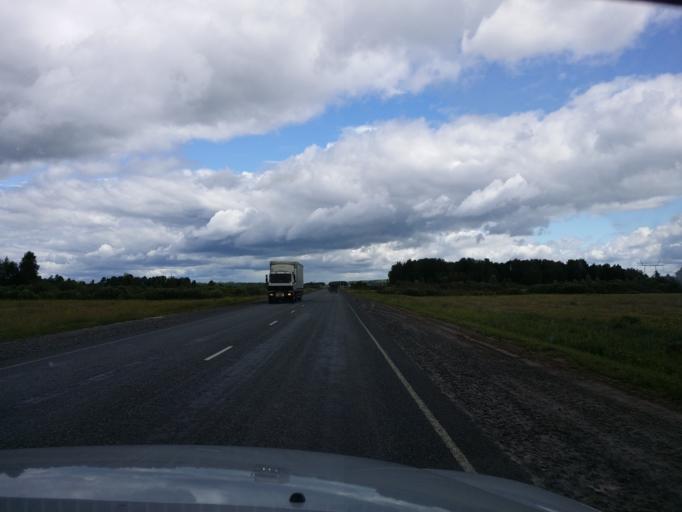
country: RU
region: Tjumen
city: Sumkino
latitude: 57.8869
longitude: 68.1107
